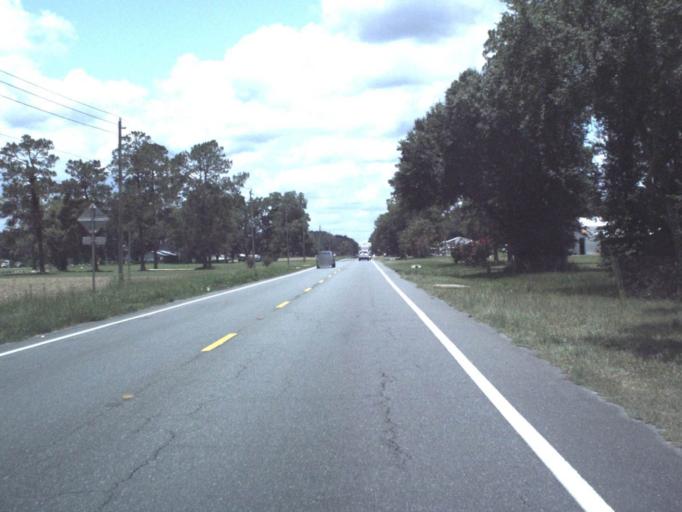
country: US
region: Florida
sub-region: Bradford County
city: Starke
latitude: 30.0313
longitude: -82.1598
